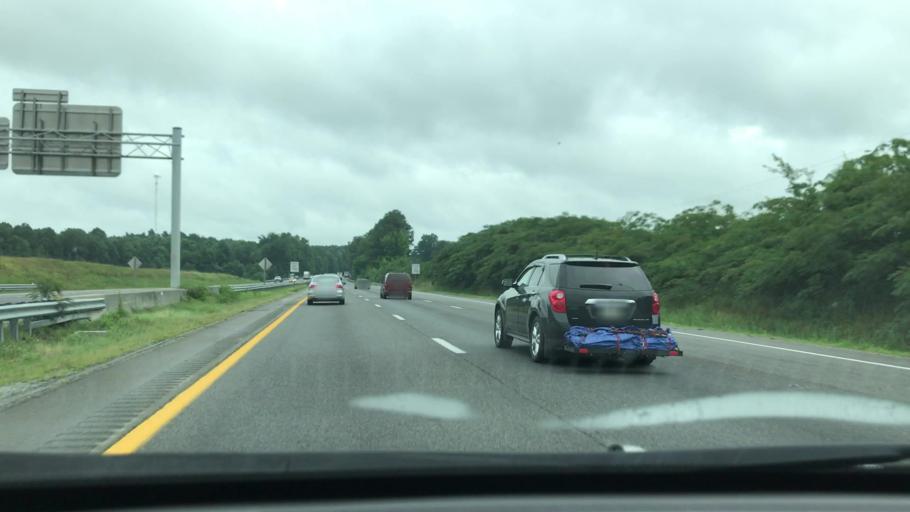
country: US
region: Virginia
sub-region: City of Emporia
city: Emporia
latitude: 36.7050
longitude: -77.5481
